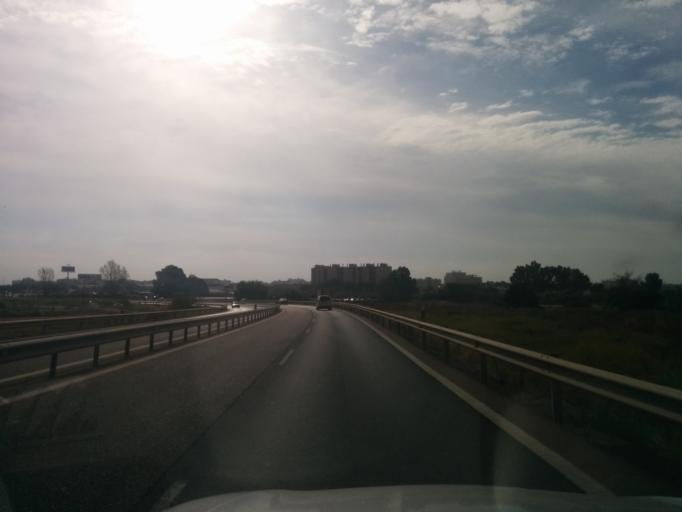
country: ES
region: Andalusia
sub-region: Provincia de Sevilla
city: Sevilla
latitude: 37.4145
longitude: -5.9407
